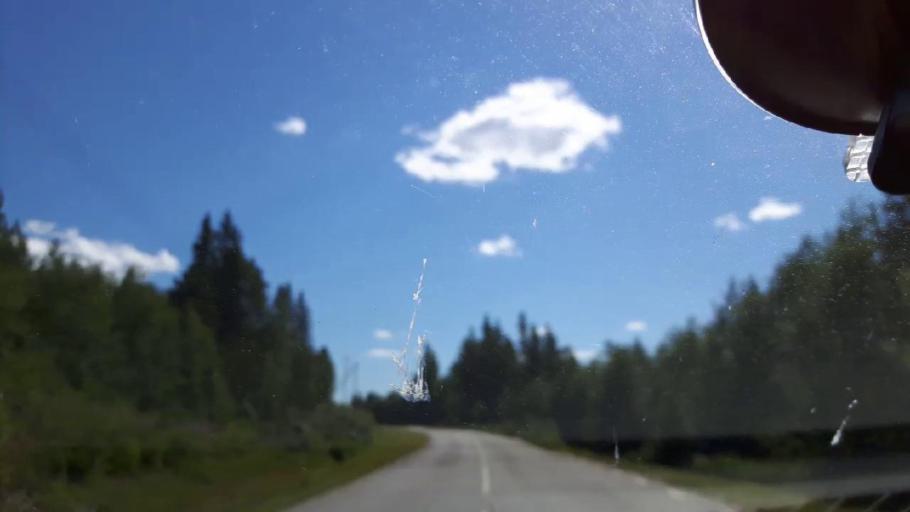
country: SE
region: Vaesternorrland
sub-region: Ange Kommun
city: Fransta
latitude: 62.7326
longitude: 16.3290
